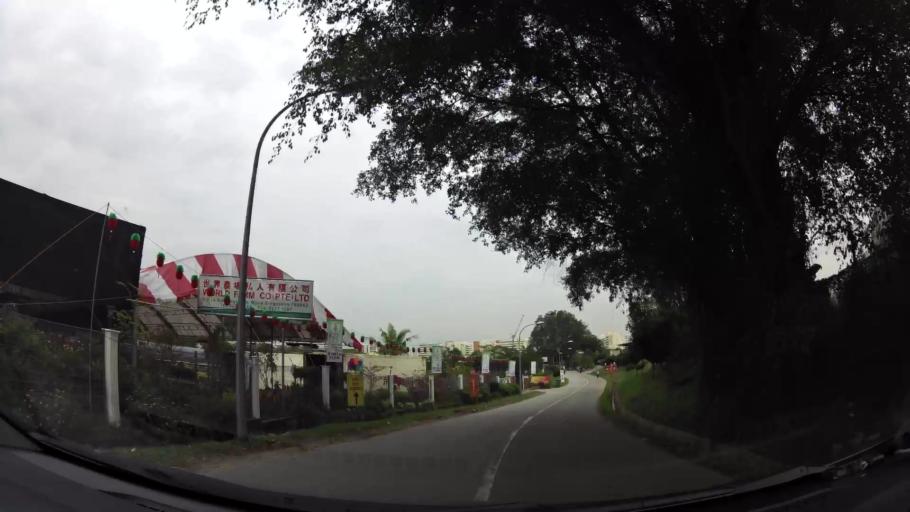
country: MY
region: Johor
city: Kampung Pasir Gudang Baru
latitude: 1.4200
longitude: 103.8266
